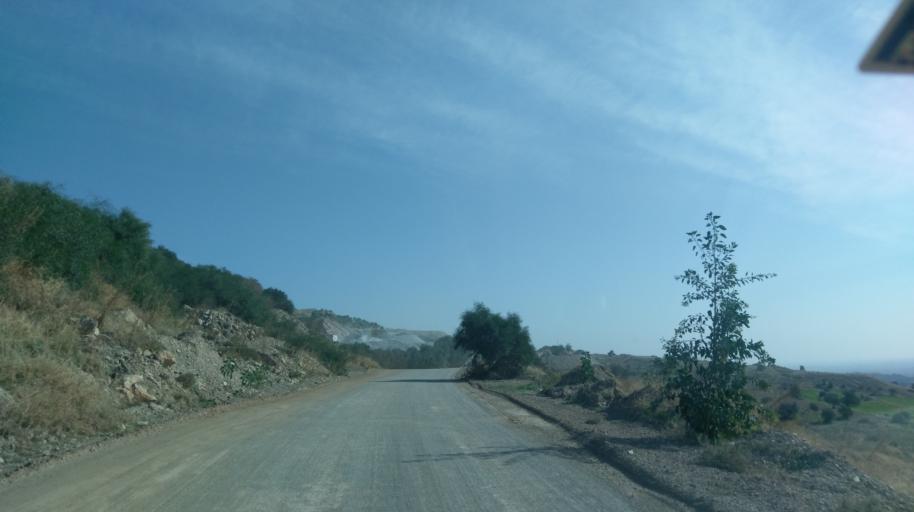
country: CY
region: Lefkosia
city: Nicosia
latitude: 35.2674
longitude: 33.4271
